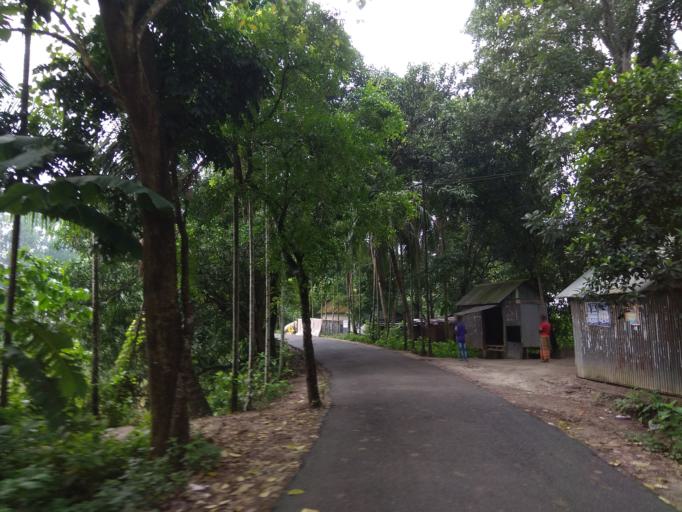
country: BD
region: Dhaka
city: Dohar
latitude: 23.4693
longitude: 90.0766
